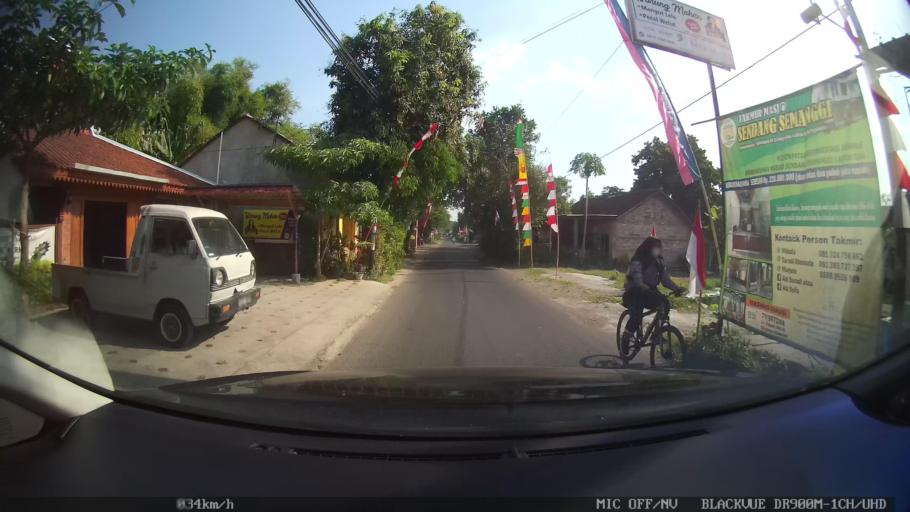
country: ID
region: Daerah Istimewa Yogyakarta
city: Kasihan
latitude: -7.8396
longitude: 110.3344
